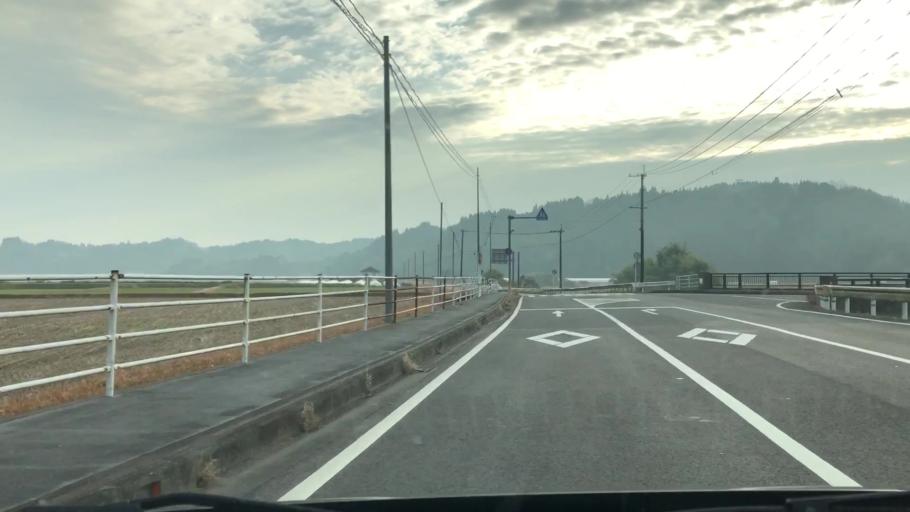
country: JP
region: Oita
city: Takedamachi
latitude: 32.9650
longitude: 131.4837
